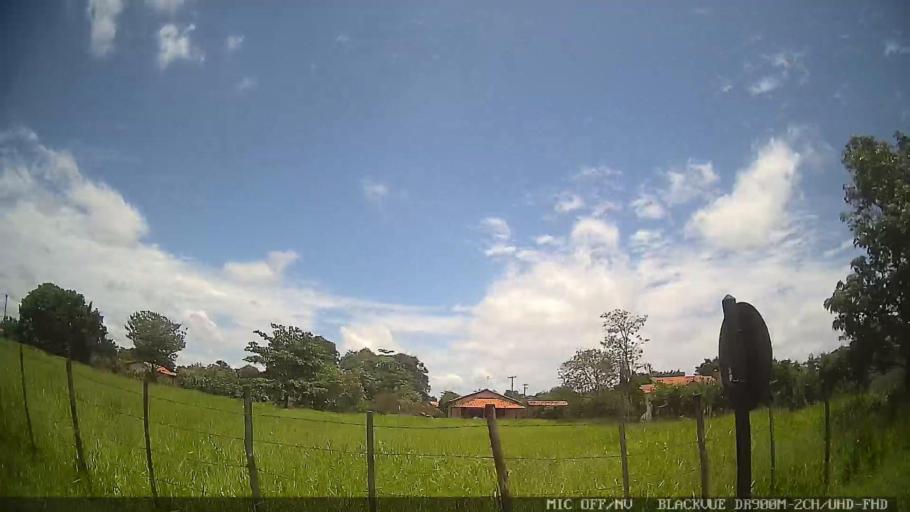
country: BR
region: Sao Paulo
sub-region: Laranjal Paulista
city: Laranjal Paulista
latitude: -23.0244
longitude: -47.8575
